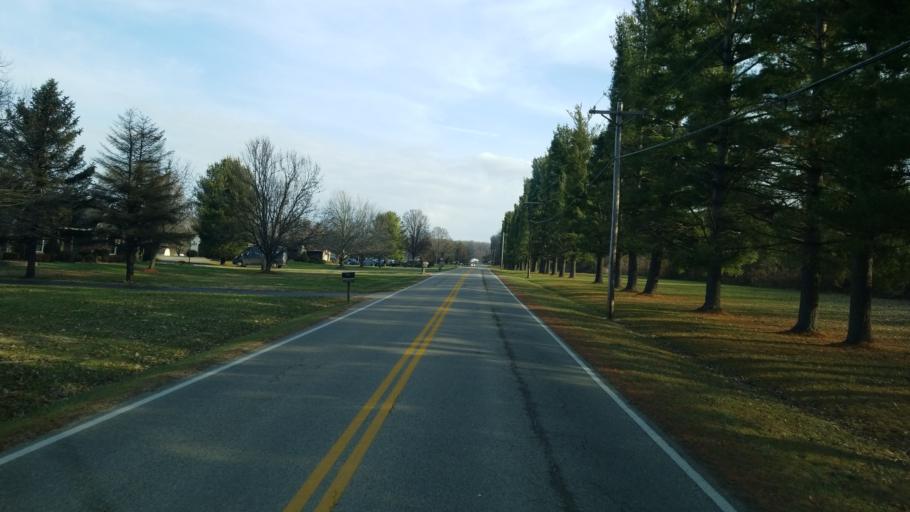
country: US
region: Ohio
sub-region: Ross County
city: Chillicothe
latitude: 39.4002
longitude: -82.9484
